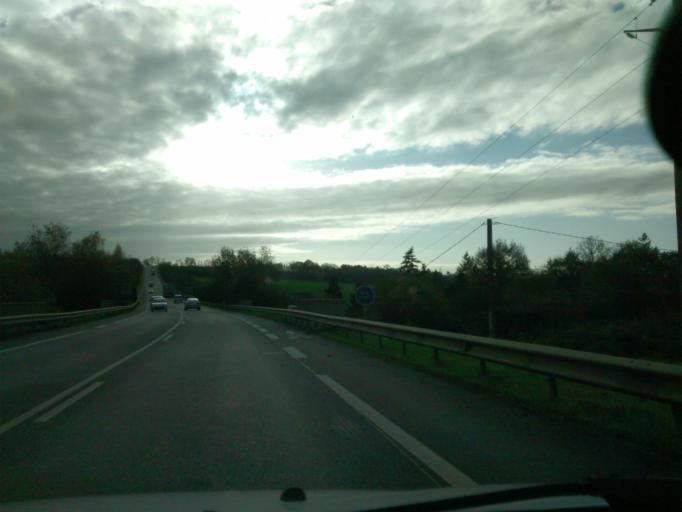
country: FR
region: Brittany
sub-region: Departement d'Ille-et-Vilaine
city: Poce-les-Bois
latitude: 48.1204
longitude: -1.2328
